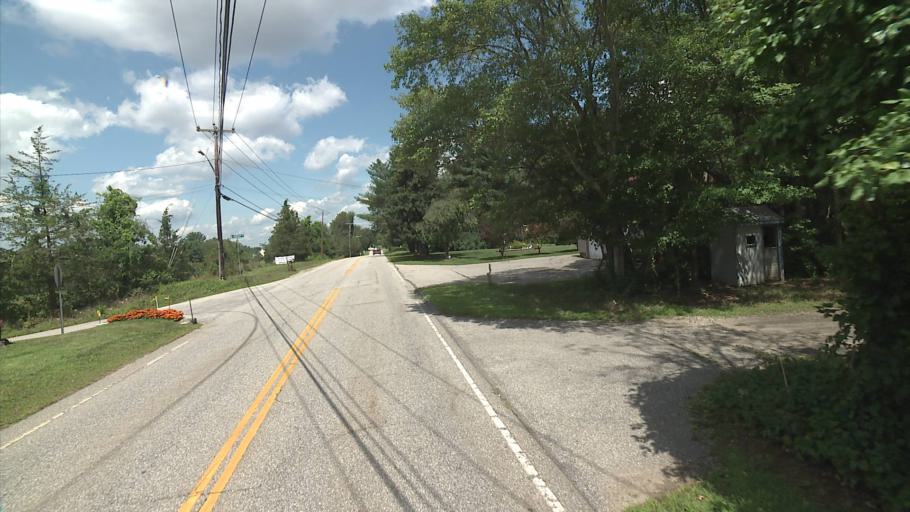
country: US
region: Connecticut
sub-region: Windham County
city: Windham
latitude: 41.7181
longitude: -72.1667
